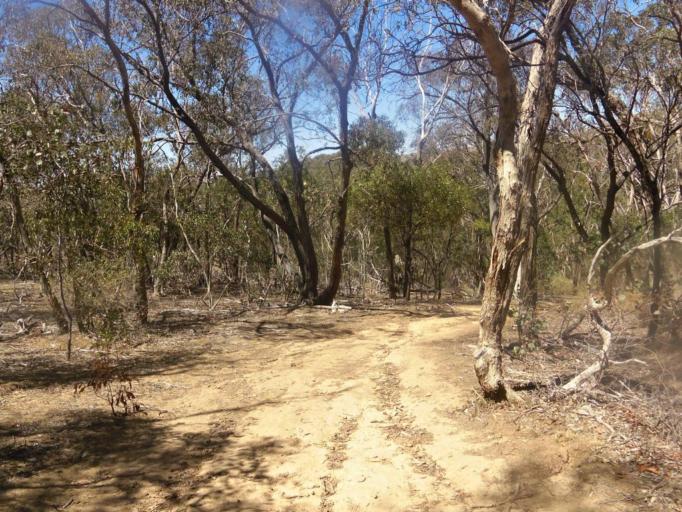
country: AU
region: Victoria
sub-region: Moorabool
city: Bacchus Marsh
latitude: -37.6637
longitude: 144.3593
